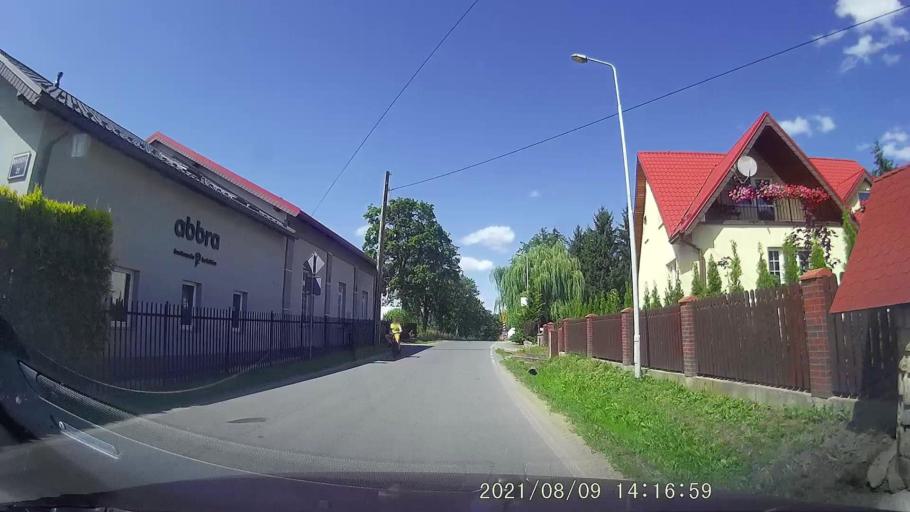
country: PL
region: Lower Silesian Voivodeship
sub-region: Powiat klodzki
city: Klodzko
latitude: 50.4623
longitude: 16.6647
